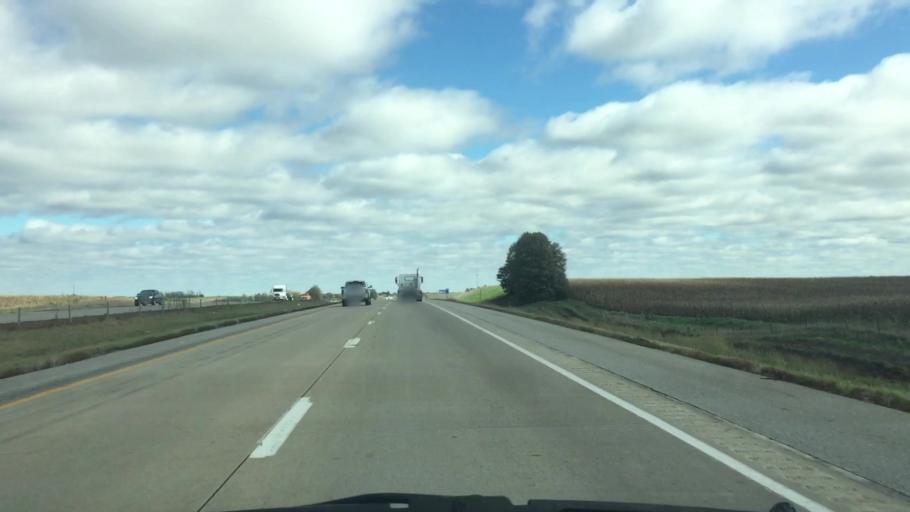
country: US
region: Iowa
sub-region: Poweshiek County
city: Brooklyn
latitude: 41.6945
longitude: -92.4992
